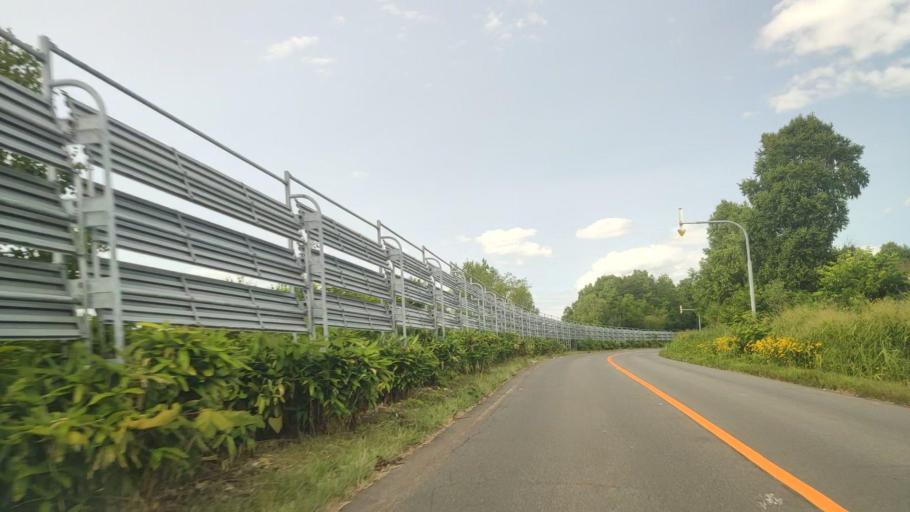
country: JP
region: Hokkaido
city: Nayoro
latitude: 44.2477
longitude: 142.4156
